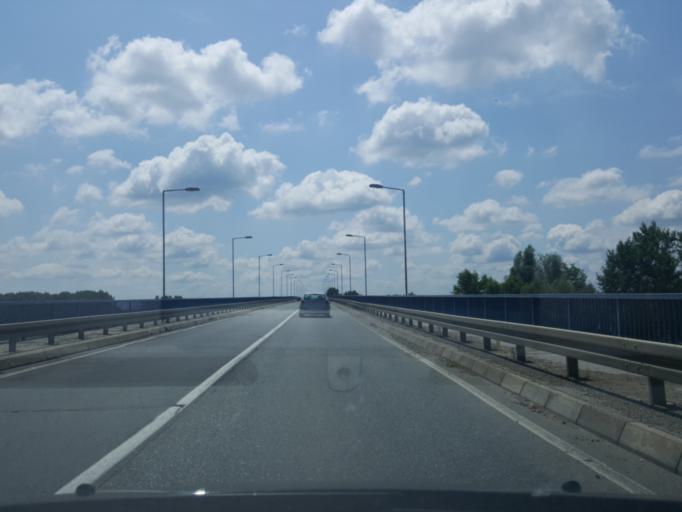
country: RS
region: Autonomna Pokrajina Vojvodina
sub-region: Sremski Okrug
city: Sremska Mitrovica
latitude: 44.9626
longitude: 19.6311
